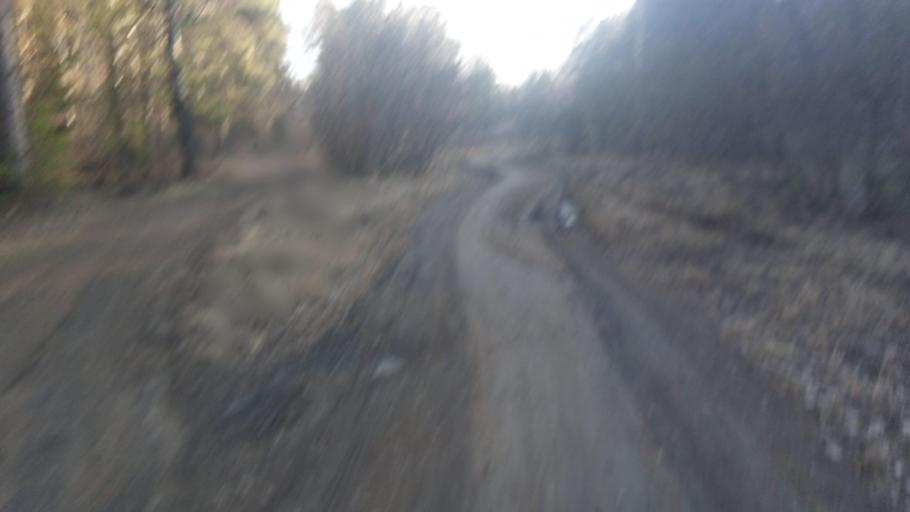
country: RU
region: Chelyabinsk
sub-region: Gorod Chelyabinsk
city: Chelyabinsk
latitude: 55.1385
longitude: 61.3291
